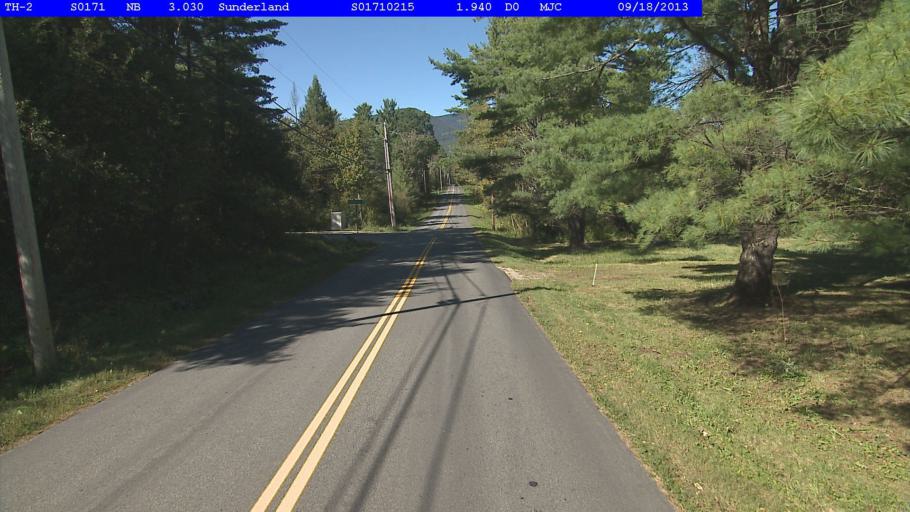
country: US
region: Vermont
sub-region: Bennington County
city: Arlington
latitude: 43.0926
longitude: -73.1238
